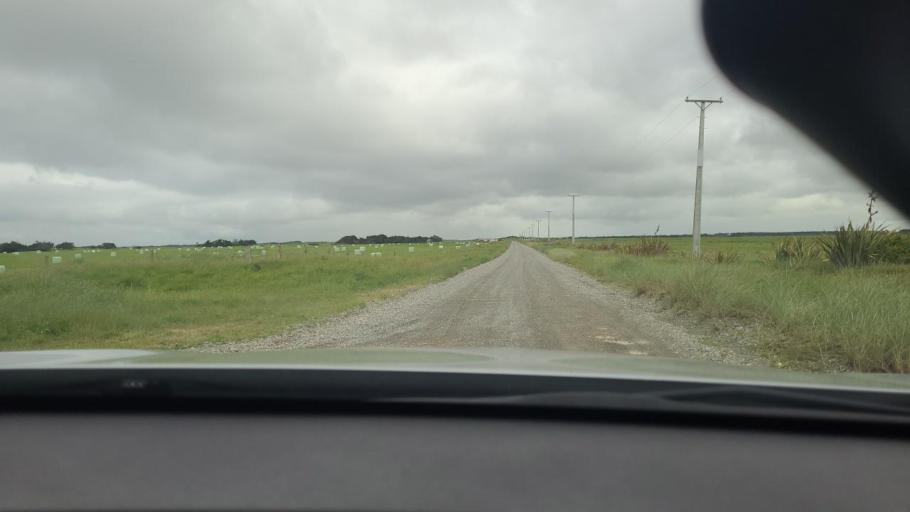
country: NZ
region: Southland
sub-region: Invercargill City
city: Invercargill
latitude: -46.3917
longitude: 168.2152
